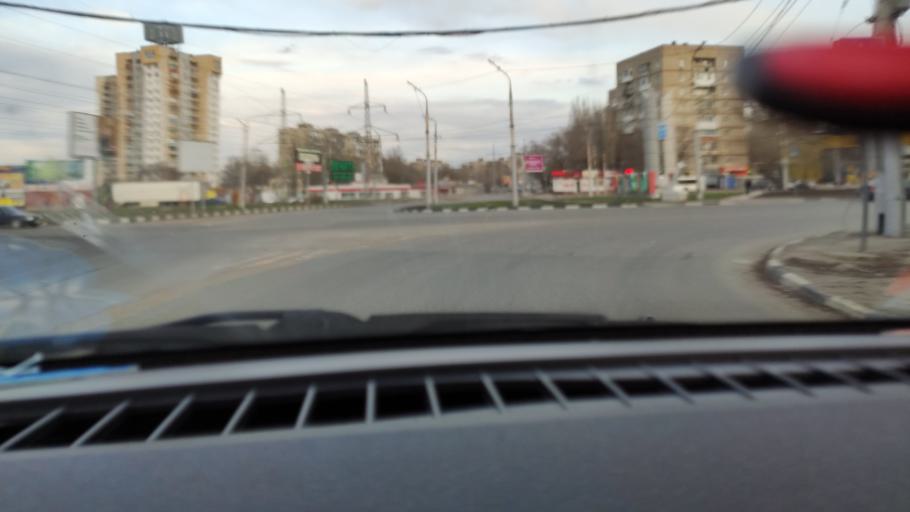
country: RU
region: Saratov
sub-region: Saratovskiy Rayon
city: Saratov
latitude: 51.6146
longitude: 45.9719
